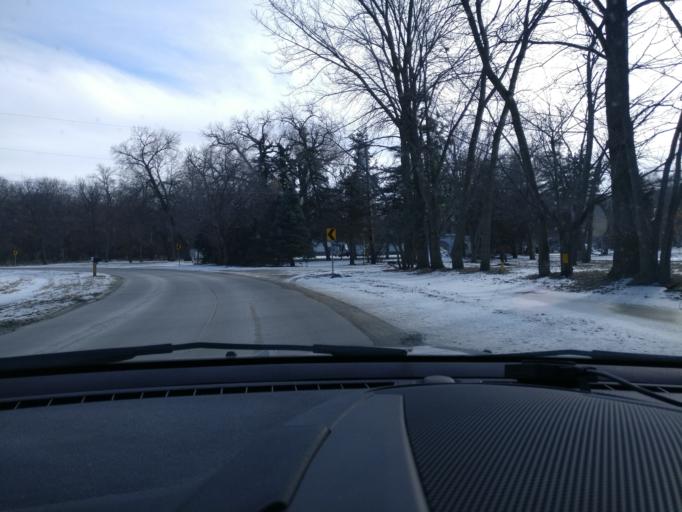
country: US
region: Nebraska
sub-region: Dodge County
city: Fremont
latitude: 41.4137
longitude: -96.5215
